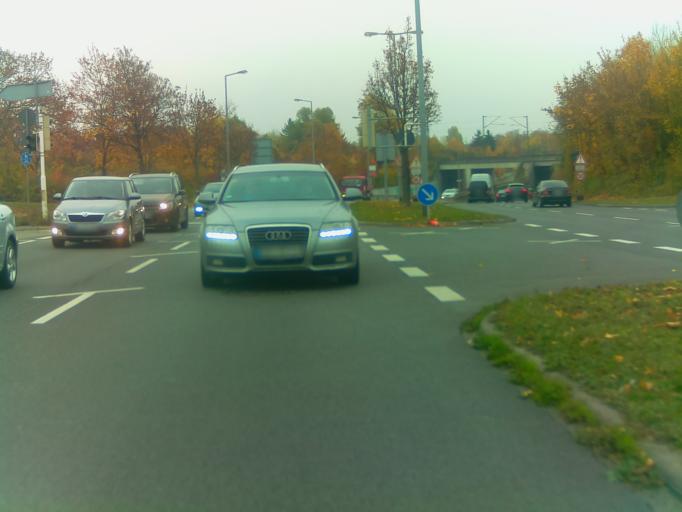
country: DE
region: Baden-Wuerttemberg
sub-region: Karlsruhe Region
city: Mannheim
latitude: 49.4703
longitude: 8.4904
